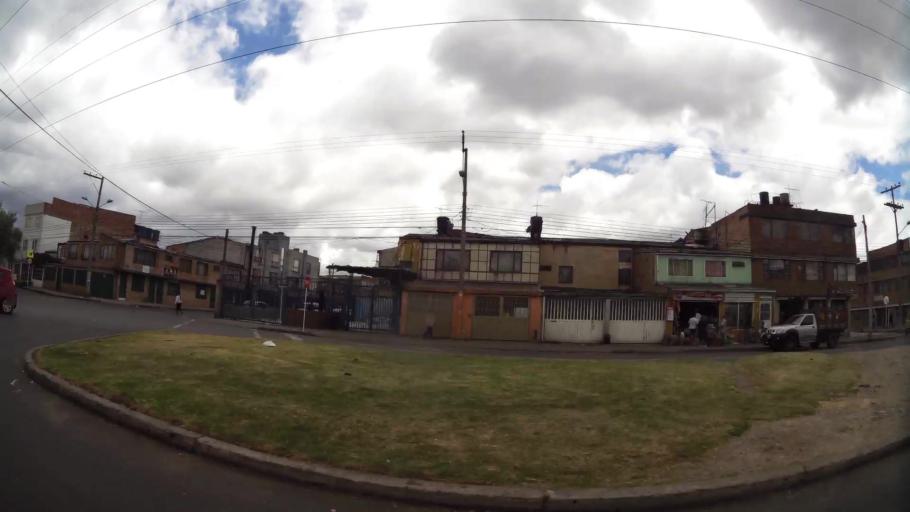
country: CO
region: Bogota D.C.
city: Bogota
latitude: 4.6143
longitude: -74.1199
